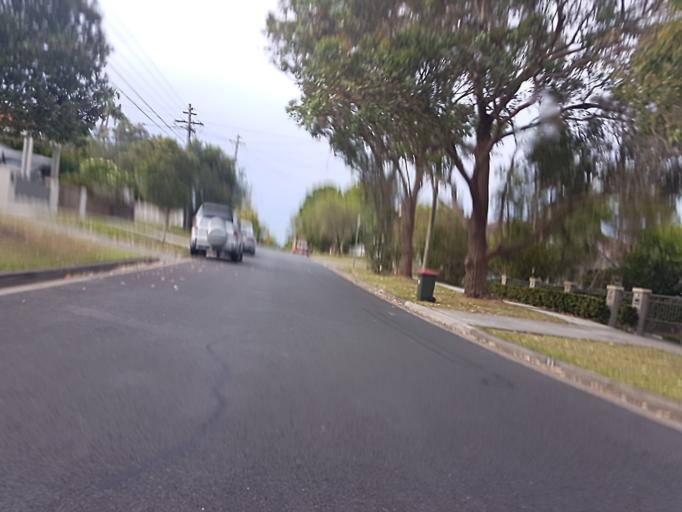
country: AU
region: New South Wales
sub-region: Willoughby
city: Castle Cove
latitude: -33.7919
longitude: 151.2037
